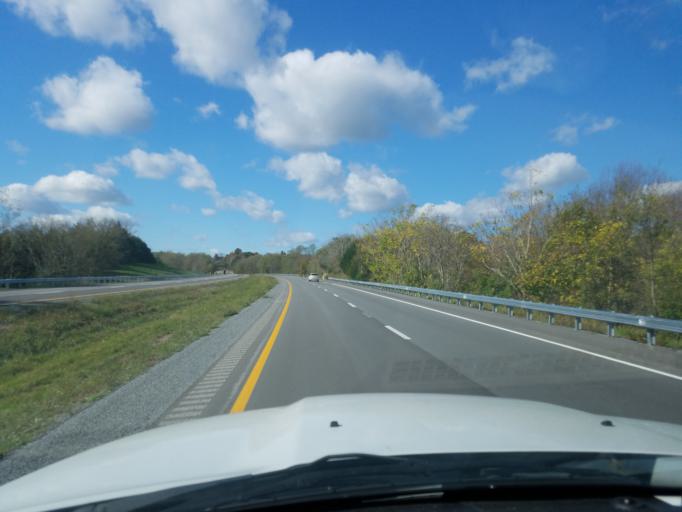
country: US
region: Kentucky
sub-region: Adair County
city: Columbia
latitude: 37.0729
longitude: -85.4050
